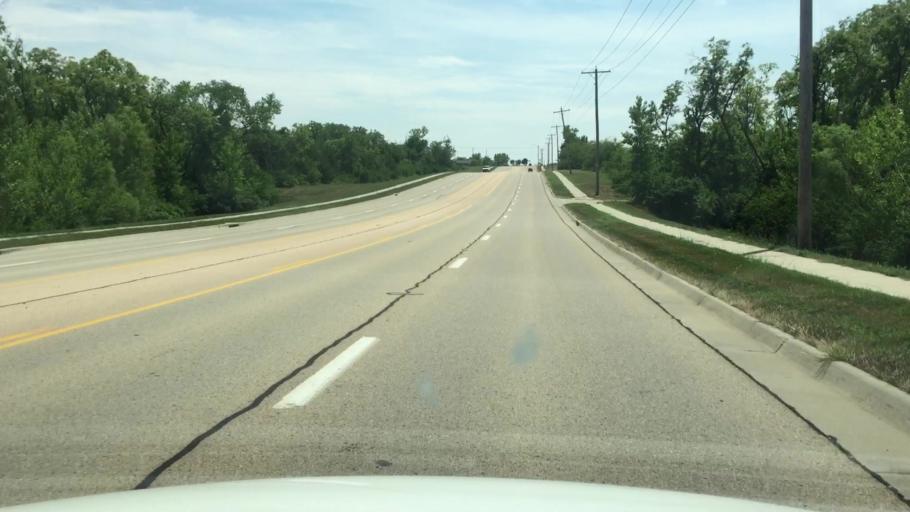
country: US
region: Kansas
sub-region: Shawnee County
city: Topeka
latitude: 38.9907
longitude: -95.6145
